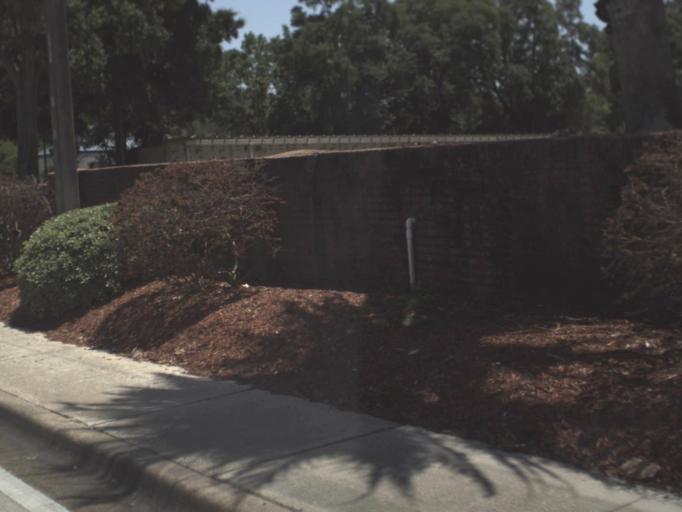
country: US
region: Florida
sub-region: Duval County
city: Jacksonville
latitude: 30.2987
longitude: -81.6201
